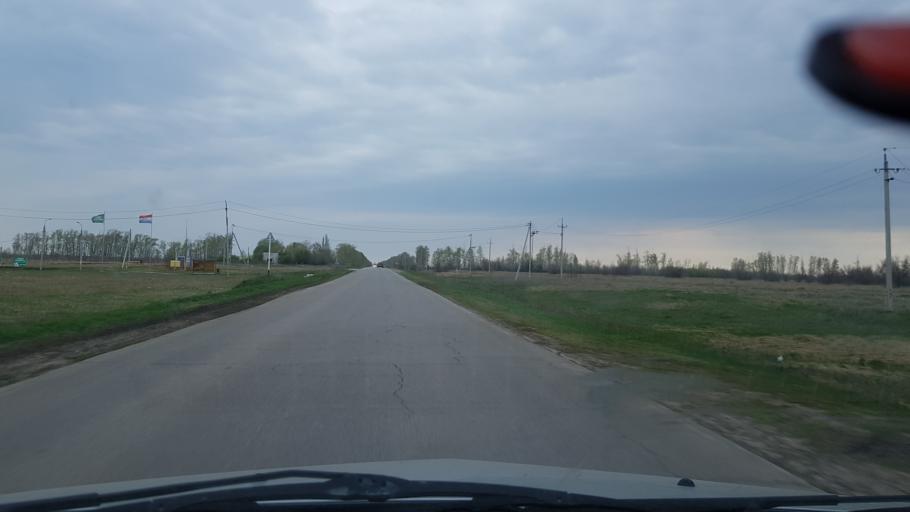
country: RU
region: Samara
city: Tol'yatti
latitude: 53.6576
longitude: 49.2491
